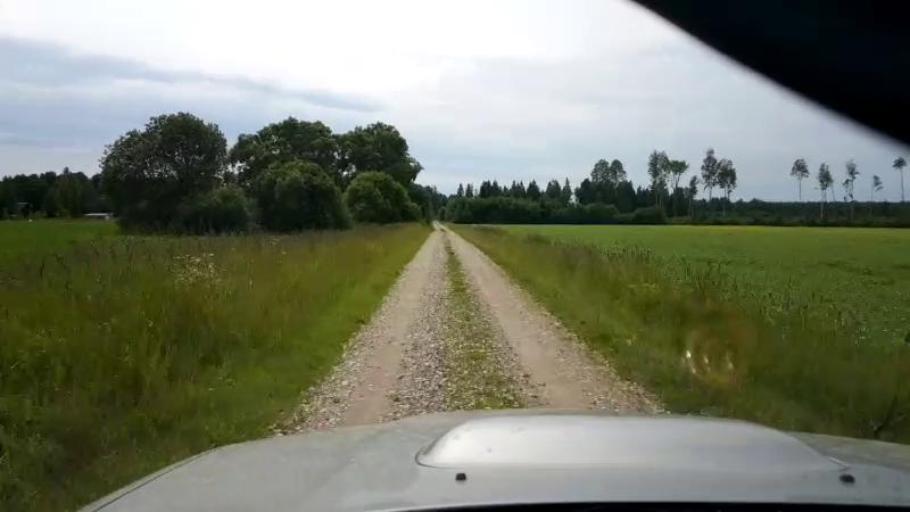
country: EE
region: Paernumaa
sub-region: Tootsi vald
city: Tootsi
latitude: 58.5583
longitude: 24.7502
